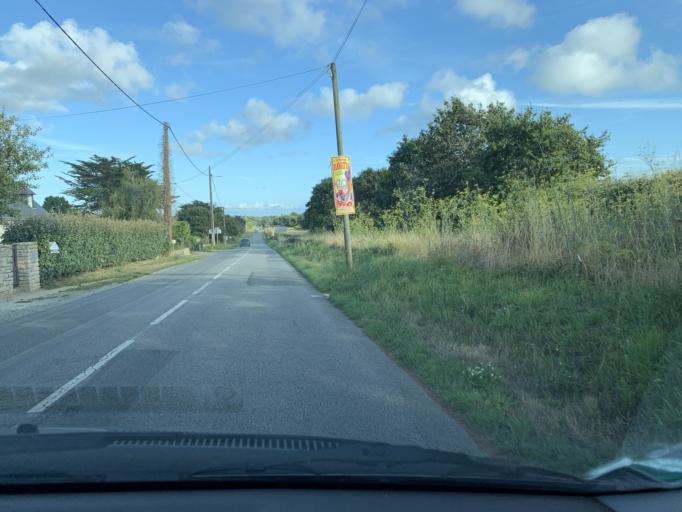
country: FR
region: Brittany
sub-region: Departement du Morbihan
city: Sarzeau
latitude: 47.5226
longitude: -2.7357
